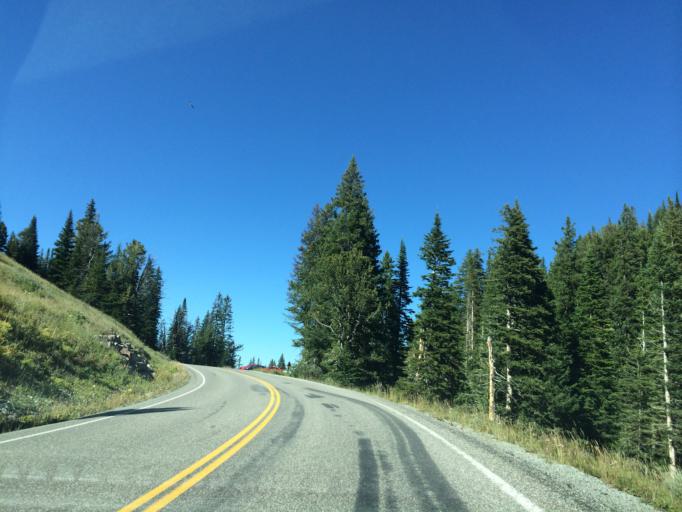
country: US
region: Montana
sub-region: Gallatin County
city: West Yellowstone
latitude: 44.7836
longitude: -110.4539
